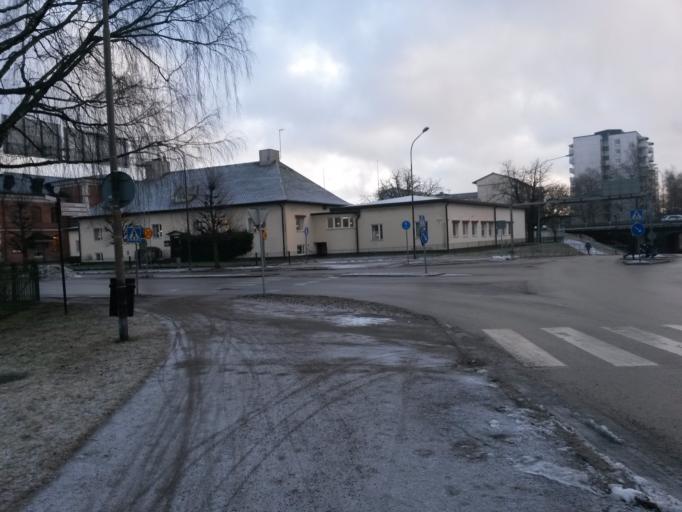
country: SE
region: Vaermland
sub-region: Karlstads Kommun
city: Karlstad
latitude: 59.3797
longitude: 13.4907
